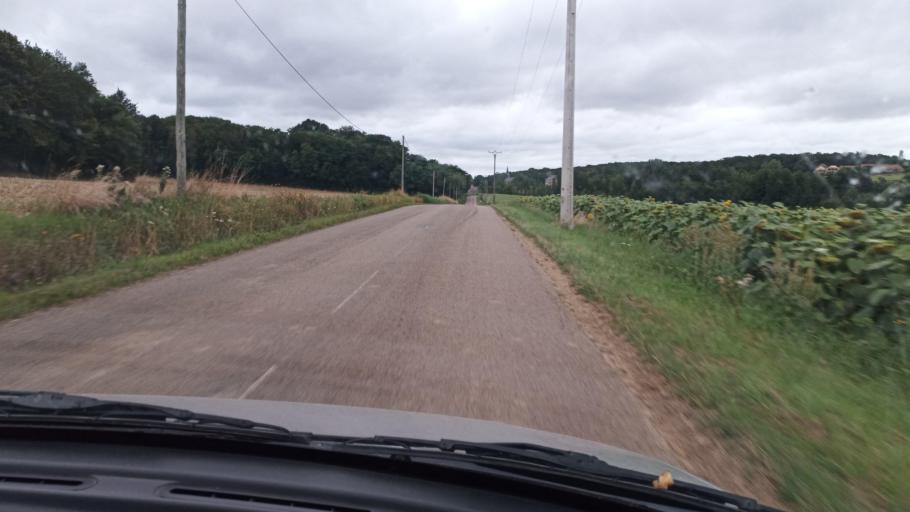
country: FR
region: Bourgogne
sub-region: Departement de l'Yonne
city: Cheroy
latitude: 48.2331
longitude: 3.0579
